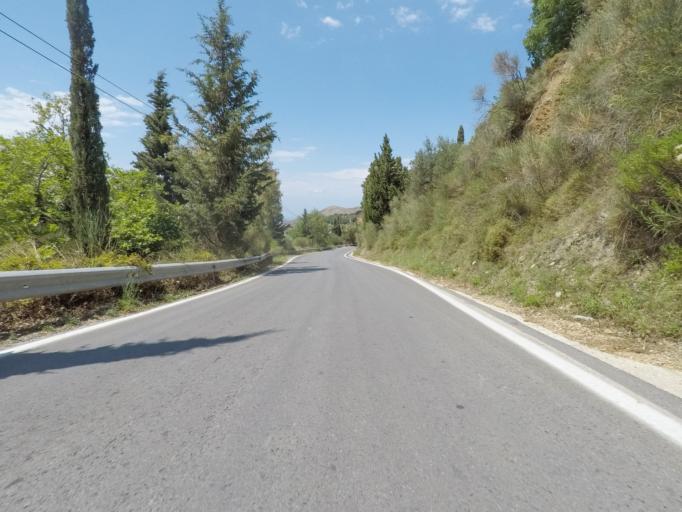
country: GR
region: Crete
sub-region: Nomos Irakleiou
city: Mokhos
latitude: 35.2225
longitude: 25.4623
